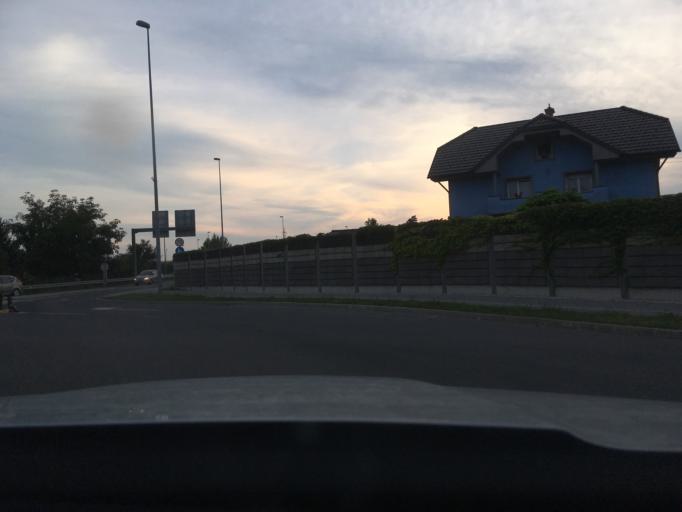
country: SI
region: Kamnik
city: Smarca
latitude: 46.1989
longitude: 14.5938
